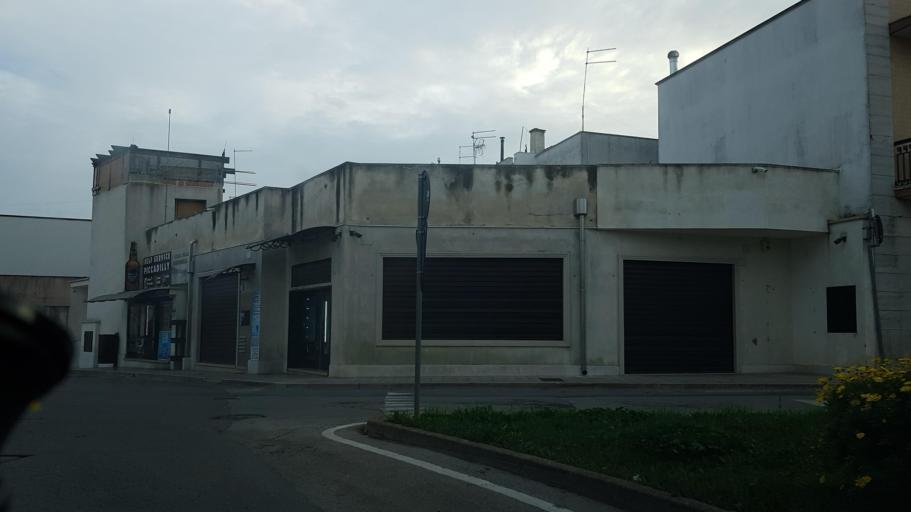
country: IT
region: Apulia
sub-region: Provincia di Brindisi
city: Latiano
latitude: 40.5567
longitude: 17.7156
